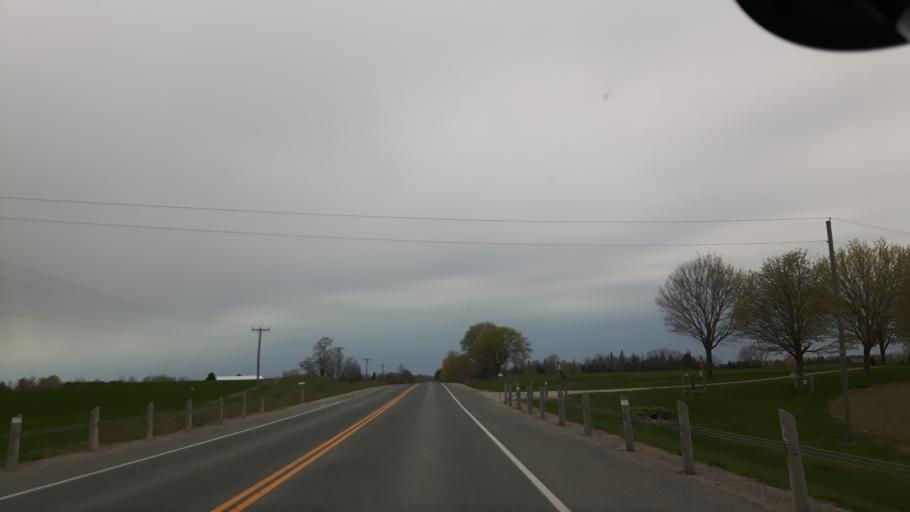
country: CA
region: Ontario
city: Bluewater
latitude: 43.6287
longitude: -81.5666
